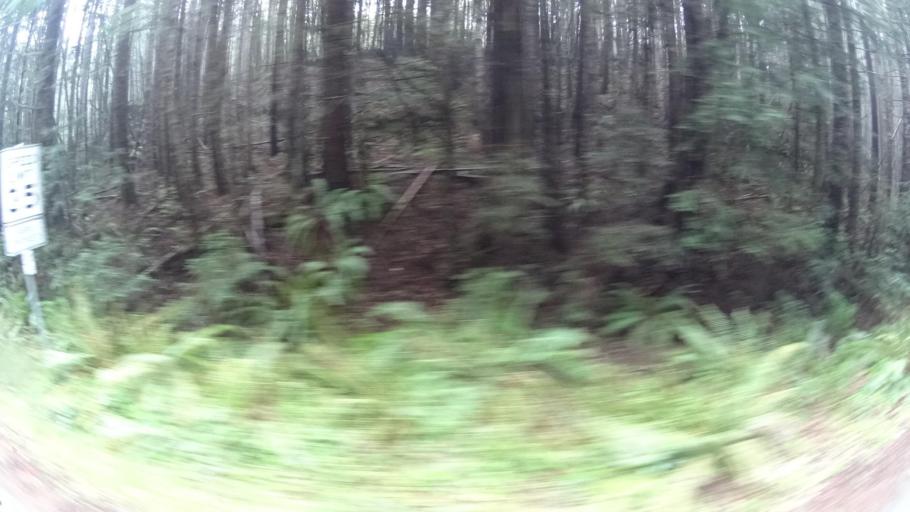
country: US
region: California
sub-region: Humboldt County
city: Westhaven-Moonstone
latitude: 41.2526
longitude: -123.9867
